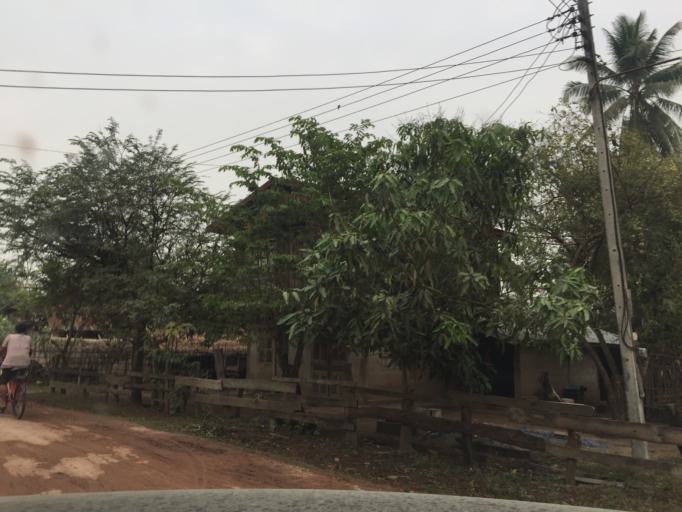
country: LA
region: Xiagnabouli
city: Sainyabuli
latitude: 19.0835
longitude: 101.5326
